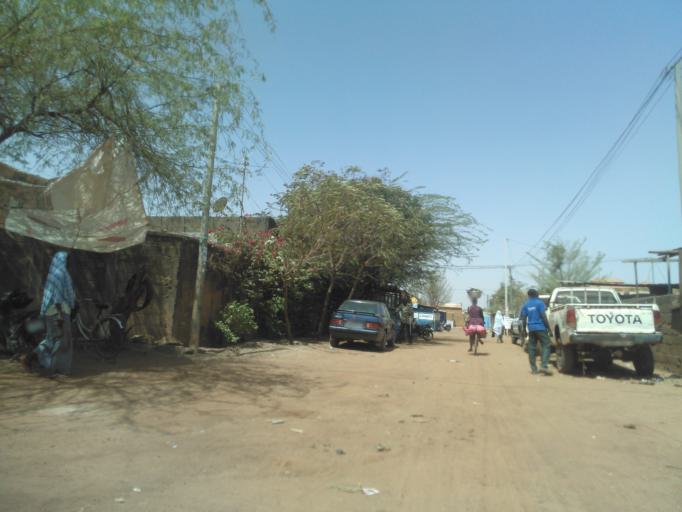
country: BF
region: Centre
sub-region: Kadiogo Province
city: Ouagadougou
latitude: 12.3912
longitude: -1.5643
